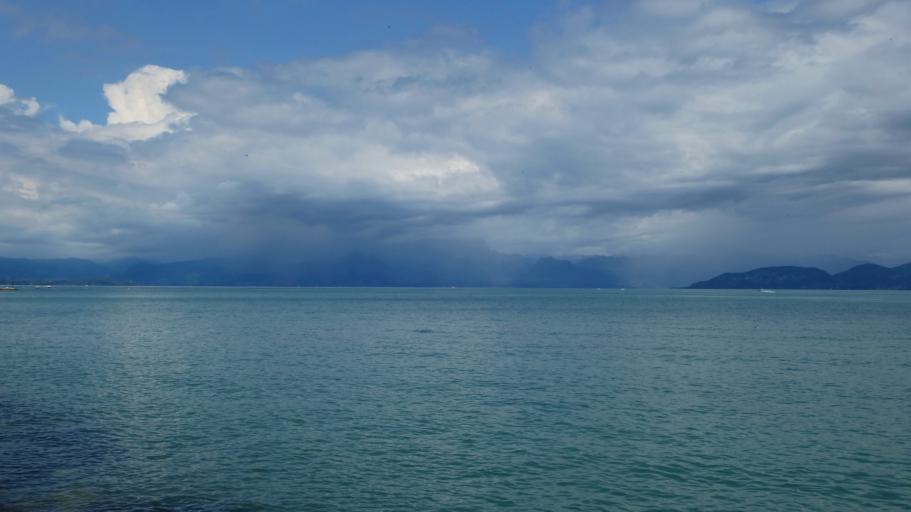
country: IT
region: Veneto
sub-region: Provincia di Verona
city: Peschiera del Garda
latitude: 45.4416
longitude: 10.6878
